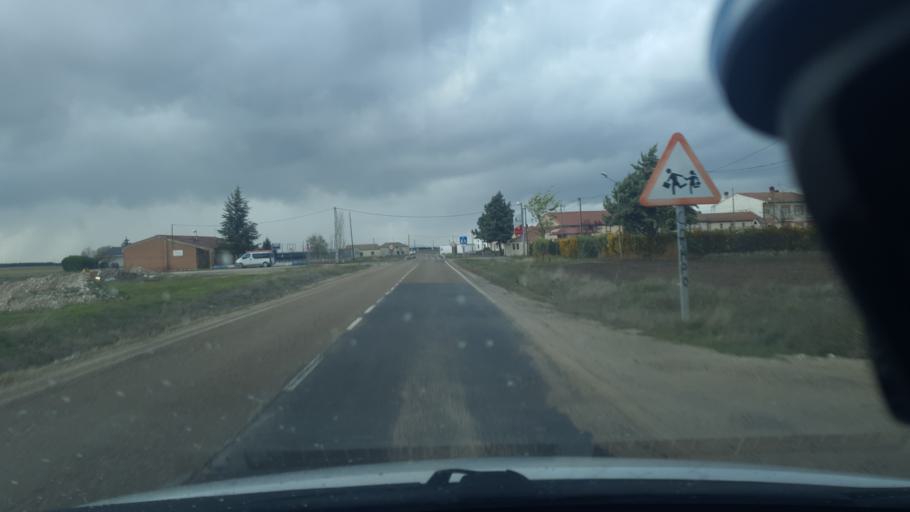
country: ES
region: Castille and Leon
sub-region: Provincia de Segovia
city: Sanchonuno
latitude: 41.3097
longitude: -4.3645
